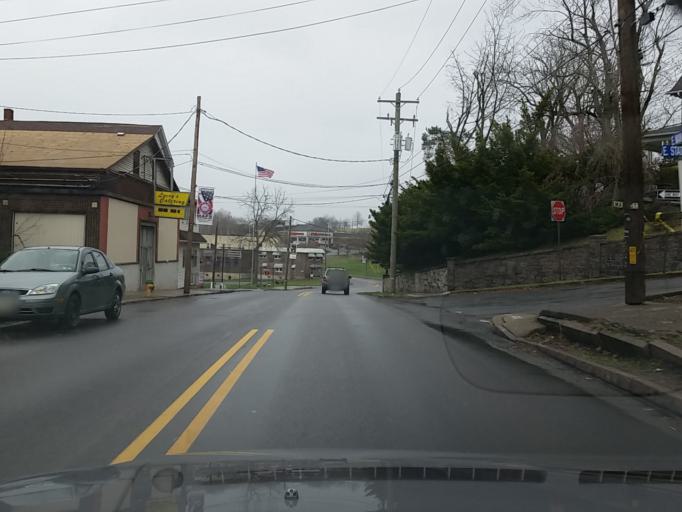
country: US
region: Pennsylvania
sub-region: Luzerne County
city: Nanticoke
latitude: 41.2061
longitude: -75.9966
